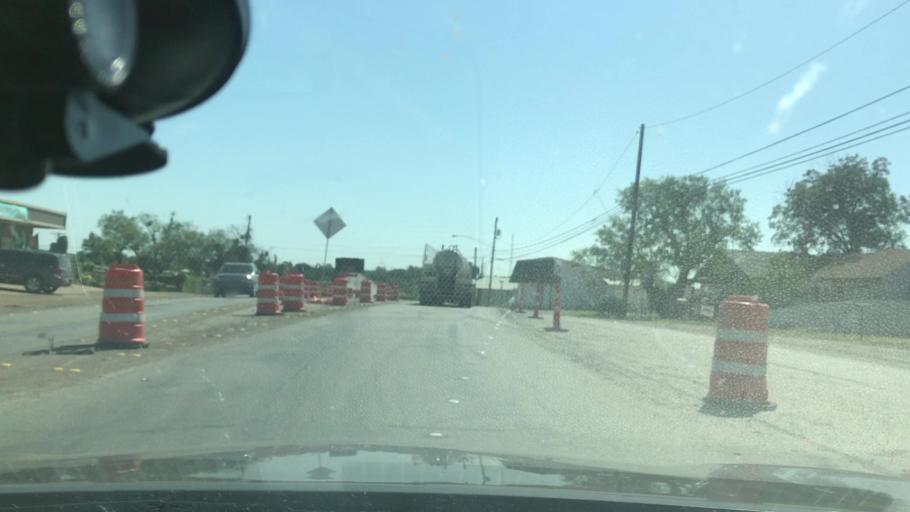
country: US
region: Texas
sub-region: Stephens County
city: Breckenridge
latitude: 32.7555
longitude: -98.8851
